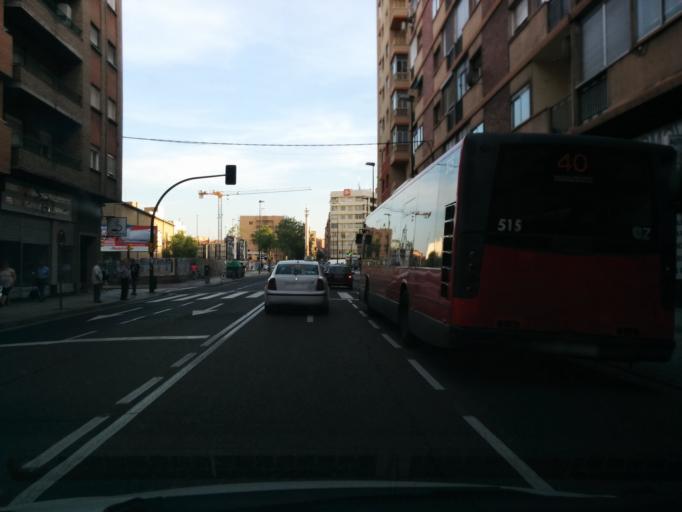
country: ES
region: Aragon
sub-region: Provincia de Zaragoza
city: Zaragoza
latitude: 41.6414
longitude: -0.8733
